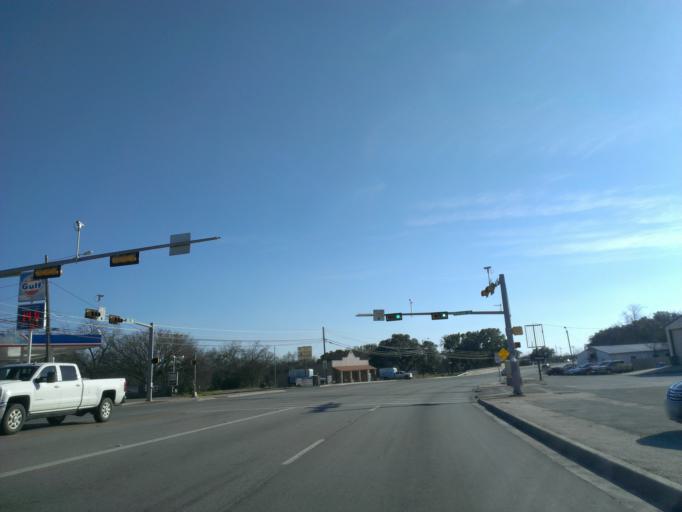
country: US
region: Texas
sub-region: Burnet County
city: Burnet
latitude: 30.7529
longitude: -98.2276
